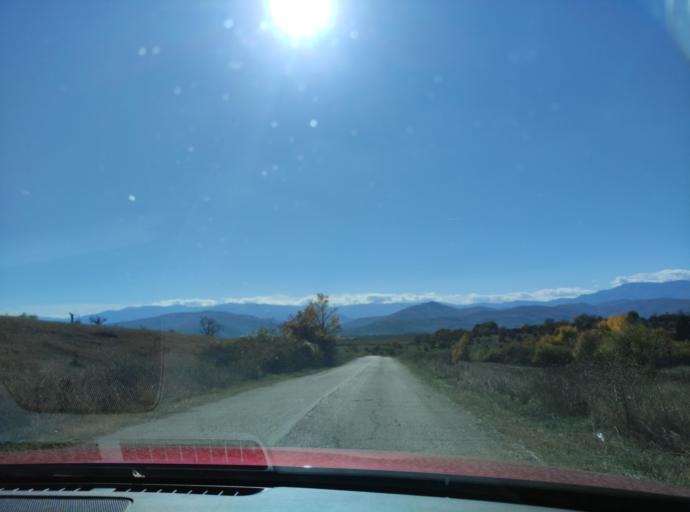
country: BG
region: Montana
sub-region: Obshtina Chiprovtsi
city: Chiprovtsi
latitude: 43.4530
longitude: 23.0472
